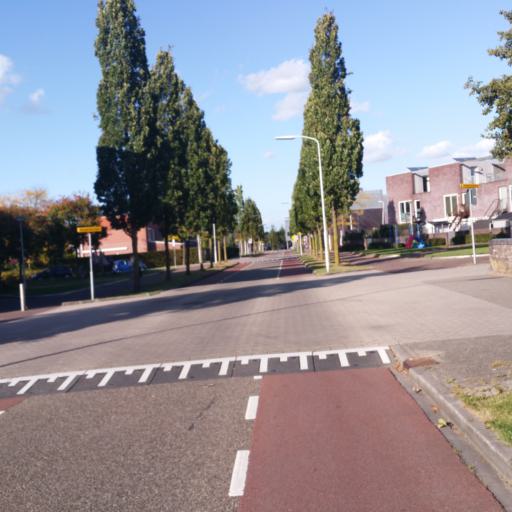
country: NL
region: Utrecht
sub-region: Gemeente IJsselstein
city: IJsselstein
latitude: 52.0094
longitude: 5.0366
